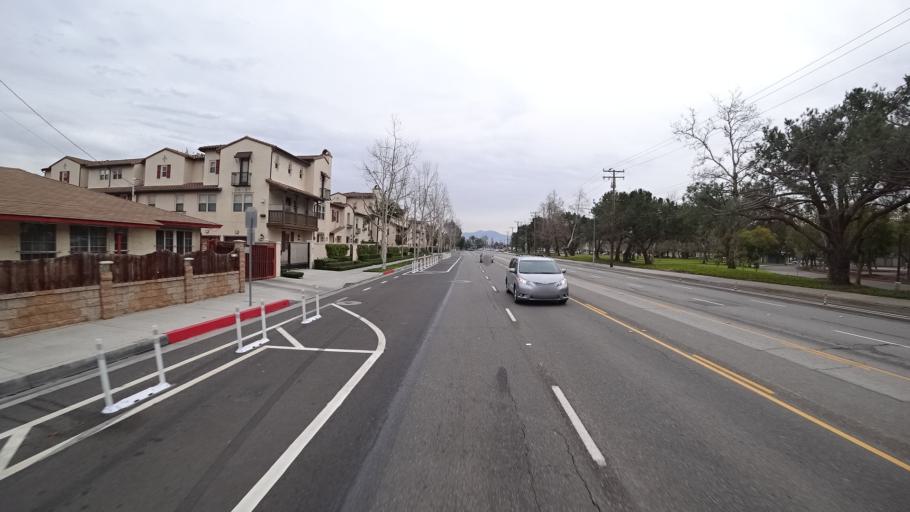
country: US
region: California
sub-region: Orange County
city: Santa Ana
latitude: 33.7276
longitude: -117.9095
